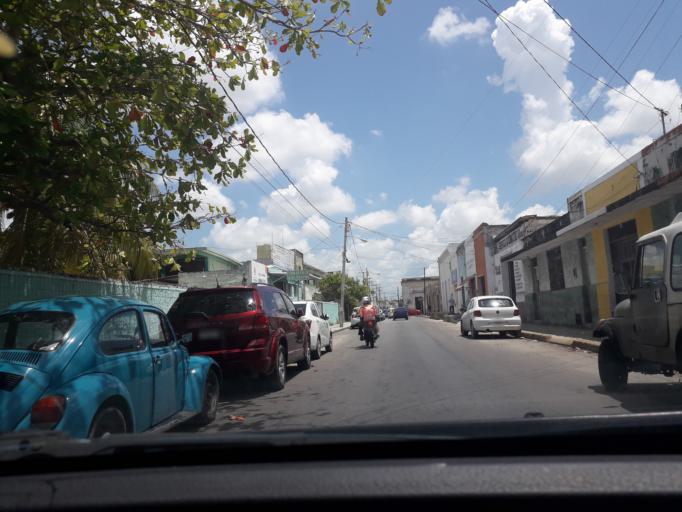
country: MX
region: Yucatan
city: Merida
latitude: 20.9583
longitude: -89.6198
